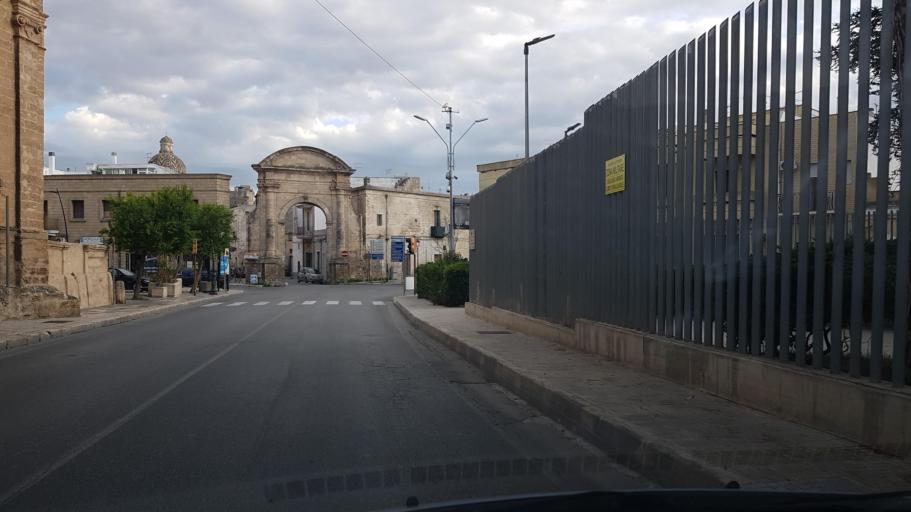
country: IT
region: Apulia
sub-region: Provincia di Brindisi
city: Francavilla Fontana
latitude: 40.5344
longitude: 17.5786
